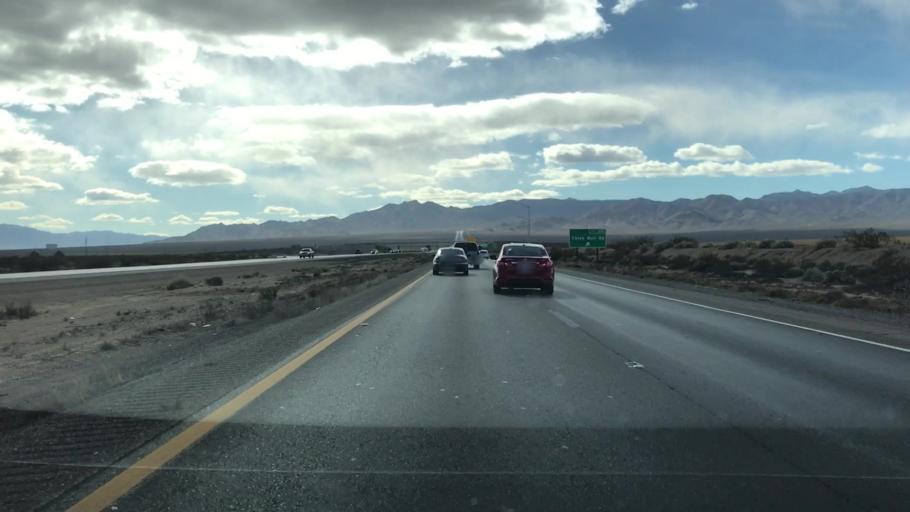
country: US
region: Nevada
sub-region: Clark County
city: Sandy Valley
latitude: 35.5459
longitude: -115.4173
